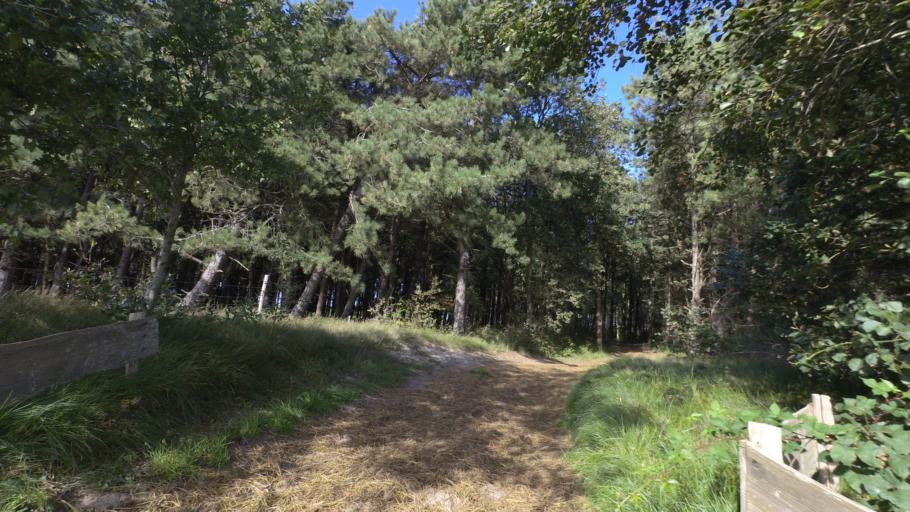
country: NL
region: Friesland
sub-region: Gemeente Ameland
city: Nes
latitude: 53.4510
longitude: 5.7125
